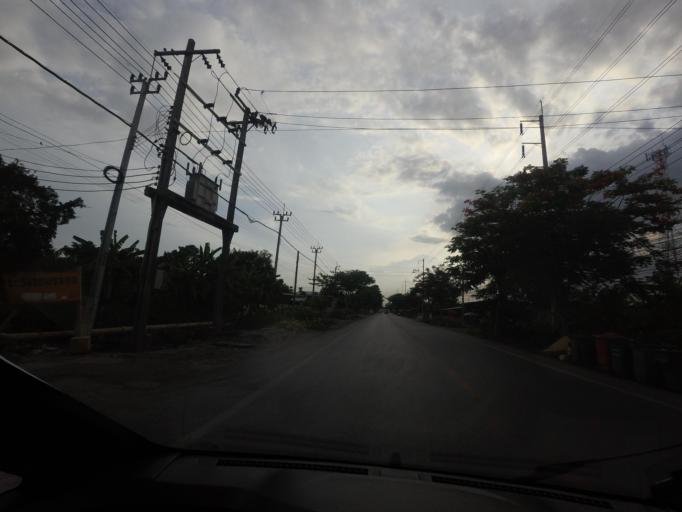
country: TH
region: Bangkok
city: Nong Chok
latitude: 13.8576
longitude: 100.8351
